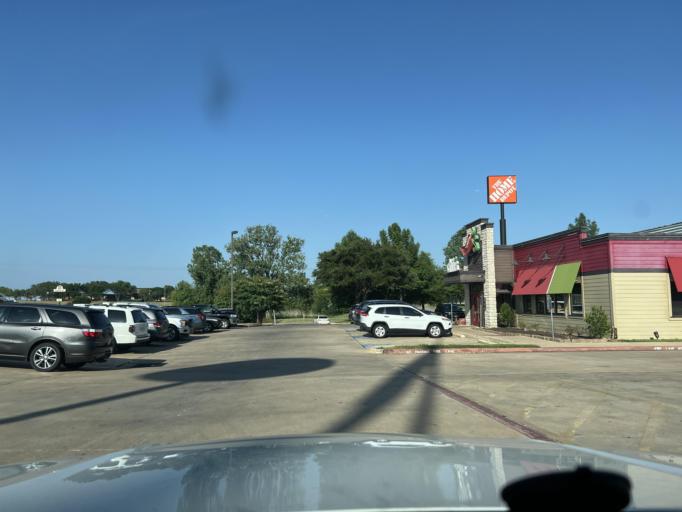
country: US
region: Texas
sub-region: Washington County
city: Brenham
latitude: 30.1419
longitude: -96.3917
